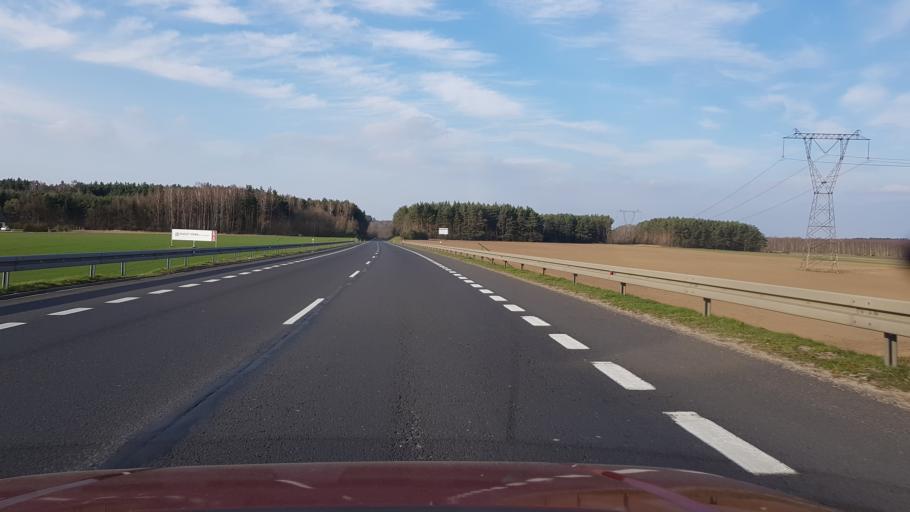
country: PL
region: West Pomeranian Voivodeship
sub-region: Powiat bialogardzki
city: Karlino
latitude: 54.0363
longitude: 15.8972
